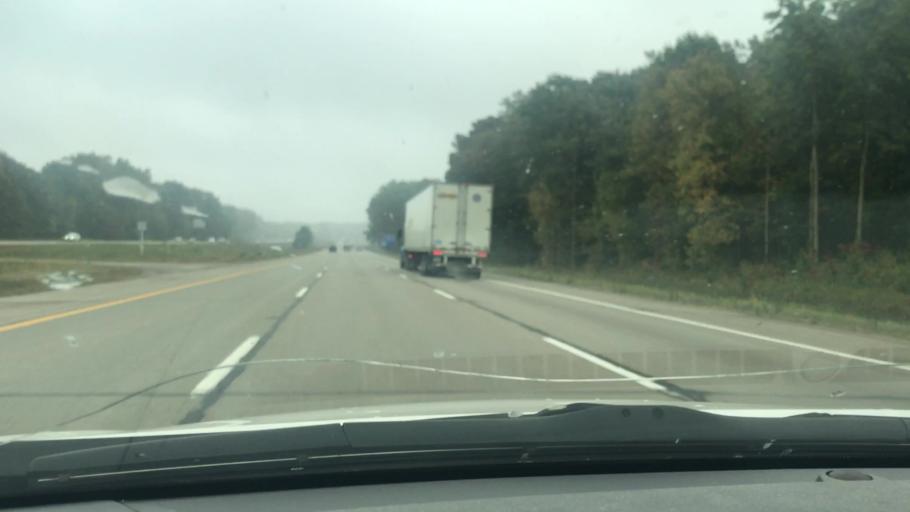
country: US
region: Michigan
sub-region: Livingston County
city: Howell
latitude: 42.6078
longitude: -83.9703
